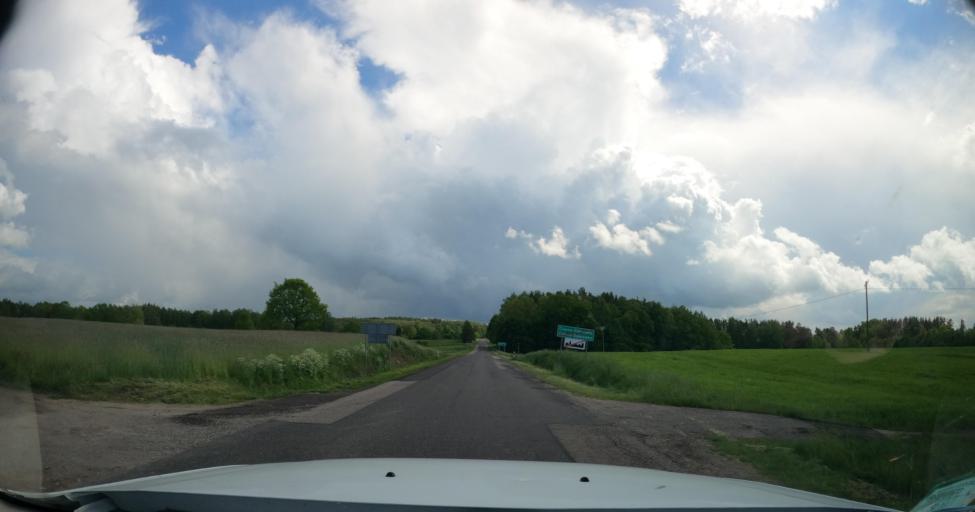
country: PL
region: Pomeranian Voivodeship
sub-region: Powiat bytowski
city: Czarna Dabrowka
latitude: 54.3529
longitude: 17.5755
